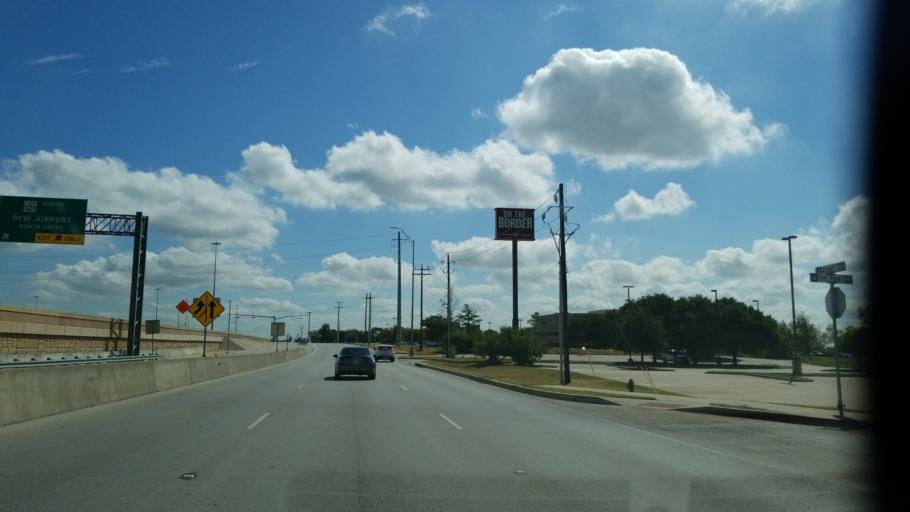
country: US
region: Texas
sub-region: Tarrant County
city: Bedford
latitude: 32.8363
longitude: -97.1293
